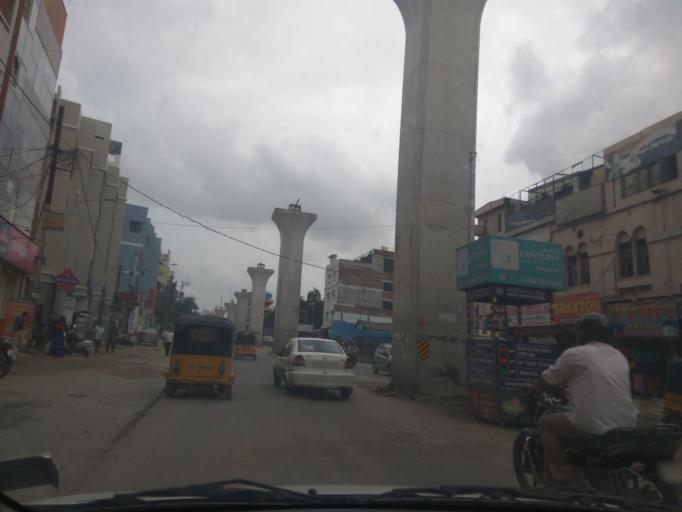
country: IN
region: Telangana
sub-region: Hyderabad
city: Hyderabad
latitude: 17.3981
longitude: 78.4932
